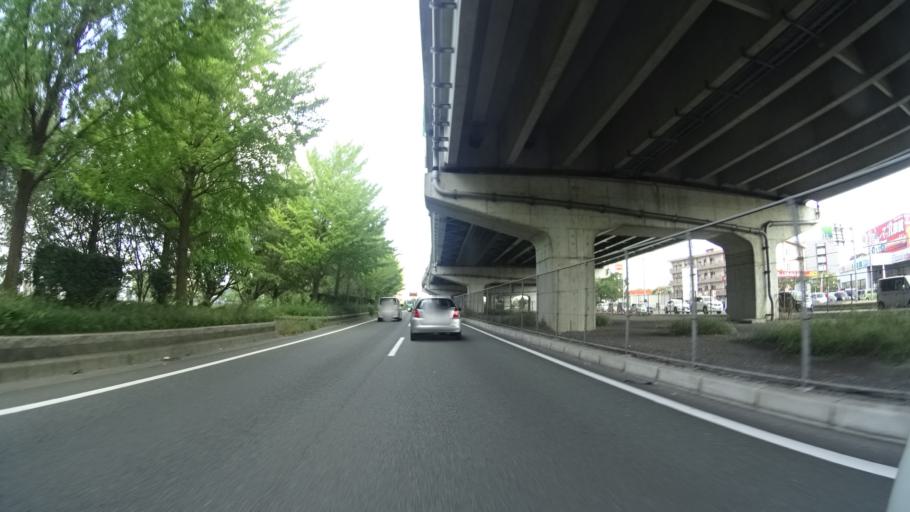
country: JP
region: Fukuoka
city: Kitakyushu
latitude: 33.8365
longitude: 130.9094
